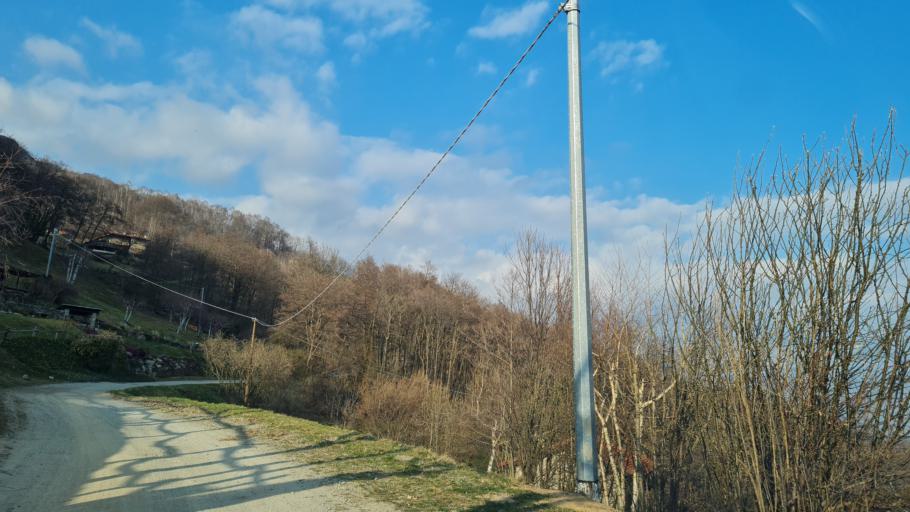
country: IT
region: Piedmont
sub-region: Provincia di Biella
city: Donato
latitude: 45.5408
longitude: 7.9069
